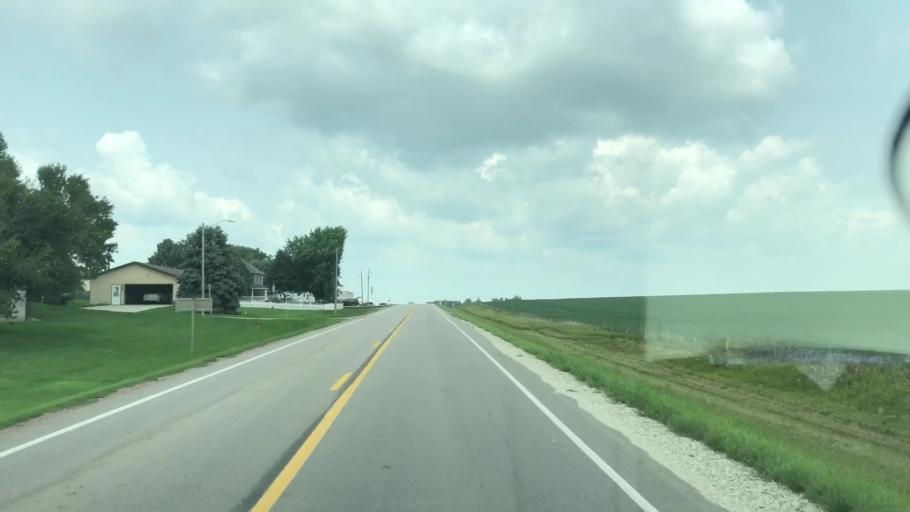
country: US
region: Iowa
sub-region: Plymouth County
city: Kingsley
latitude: 42.5907
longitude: -95.9574
